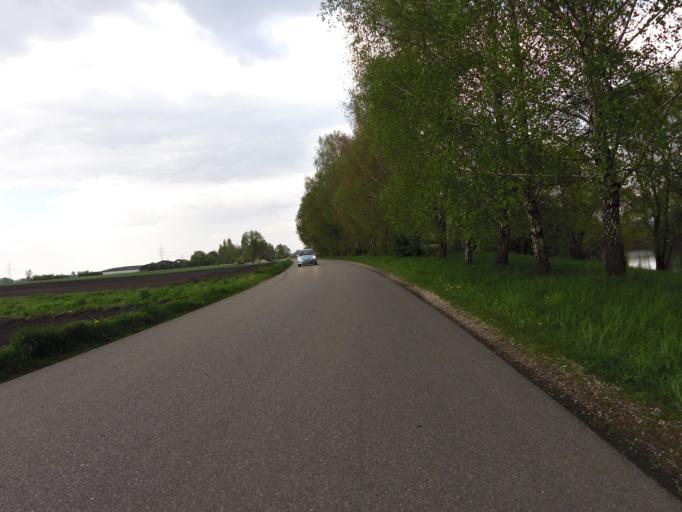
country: DE
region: Bavaria
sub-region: Upper Bavaria
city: Eitting
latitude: 48.3653
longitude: 11.8969
